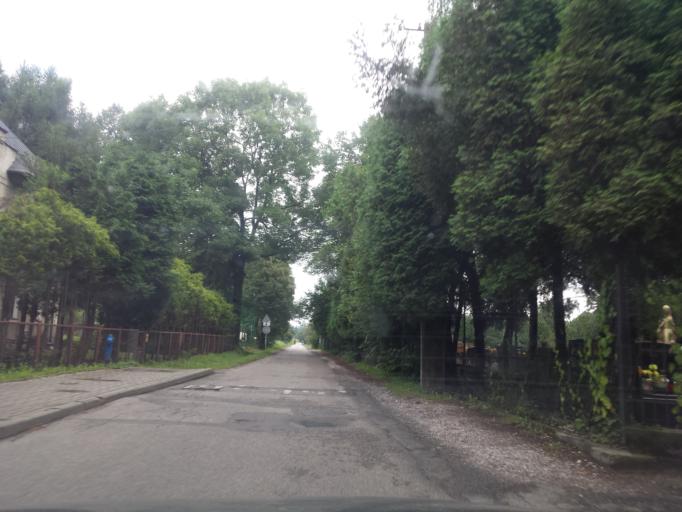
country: PL
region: Silesian Voivodeship
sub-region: Powiat bielski
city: Wilkowice
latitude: 49.7814
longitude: 19.0737
